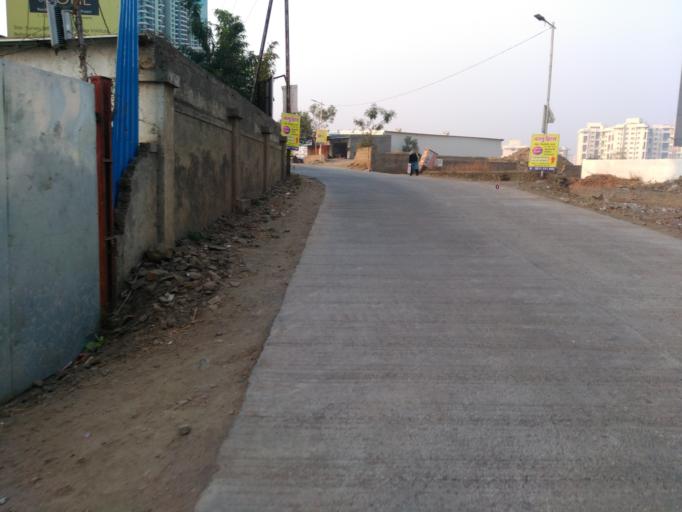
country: IN
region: Maharashtra
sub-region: Pune Division
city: Pune
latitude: 18.4532
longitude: 73.9117
